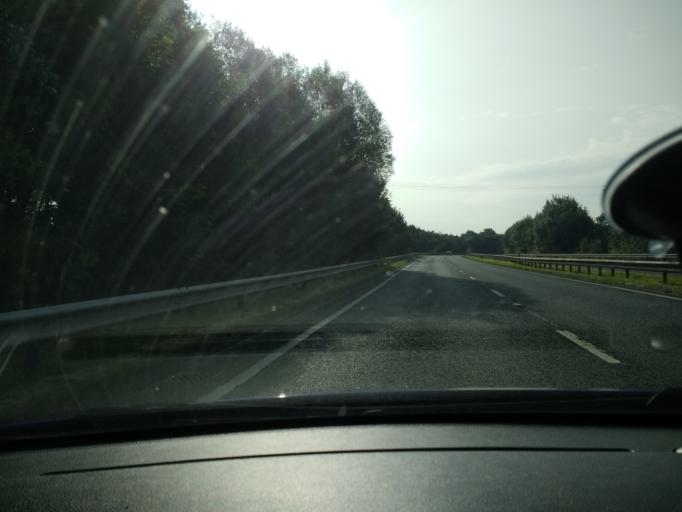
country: GB
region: England
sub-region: Cumbria
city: Milnthorpe
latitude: 54.2532
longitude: -2.7381
